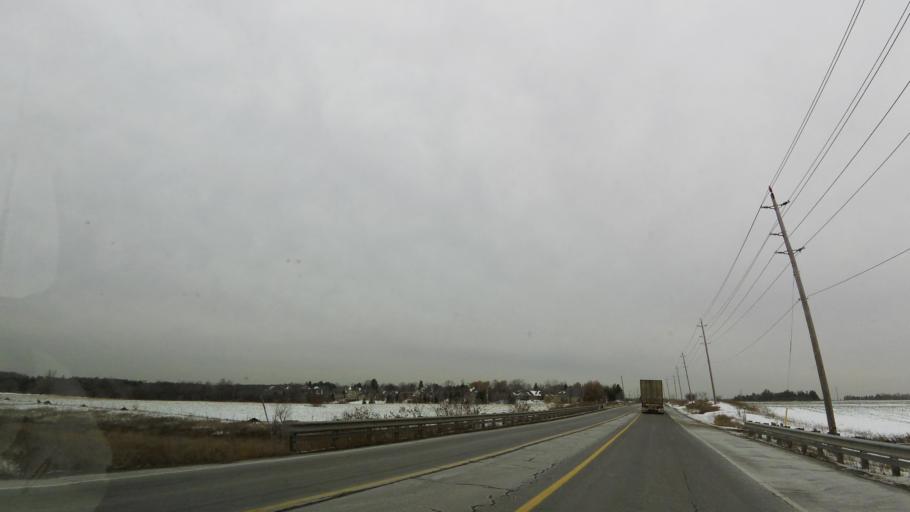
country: CA
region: Ontario
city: Vaughan
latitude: 43.9194
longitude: -79.5721
